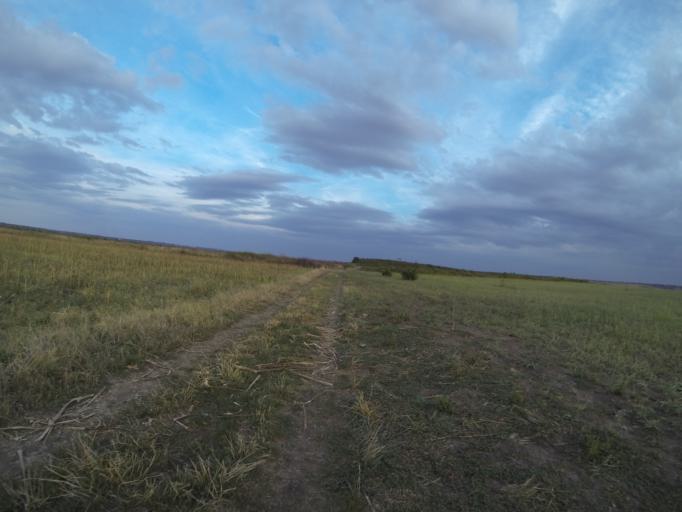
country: RO
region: Dolj
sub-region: Comuna Ceratu
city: Ceratu
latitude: 44.0955
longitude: 23.6683
